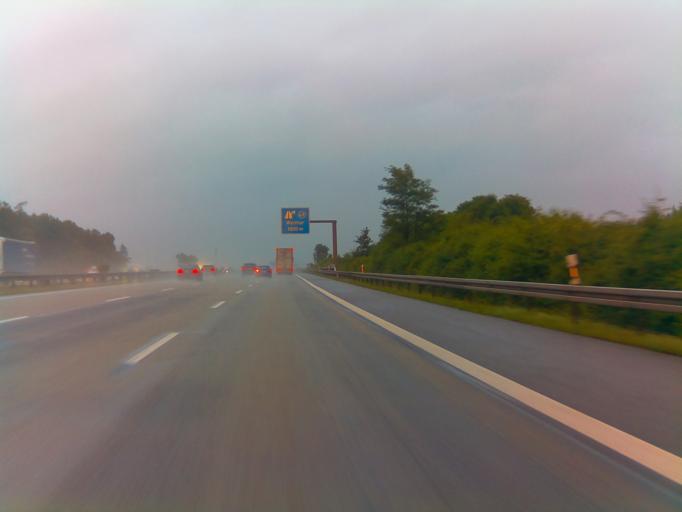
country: DE
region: Thuringia
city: Troistedt
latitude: 50.9471
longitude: 11.2783
